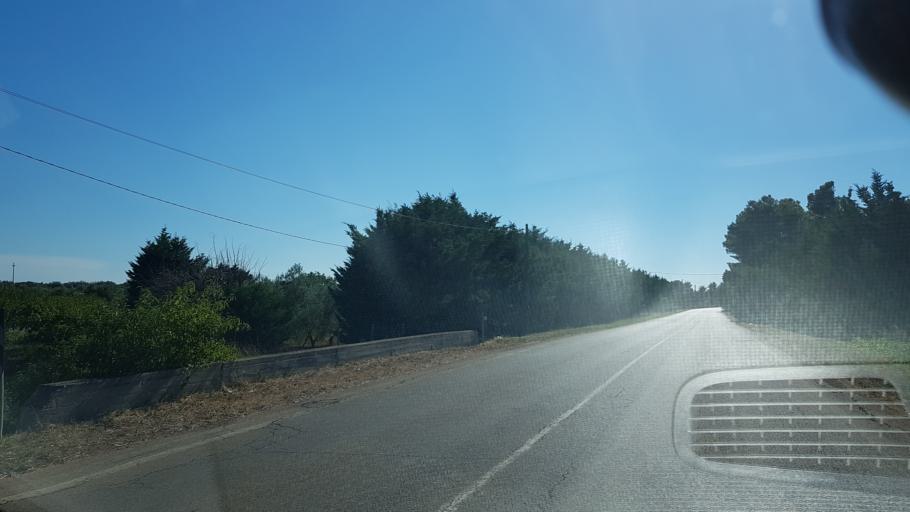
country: IT
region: Apulia
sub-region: Provincia di Brindisi
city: Mesagne
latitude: 40.5577
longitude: 17.8450
